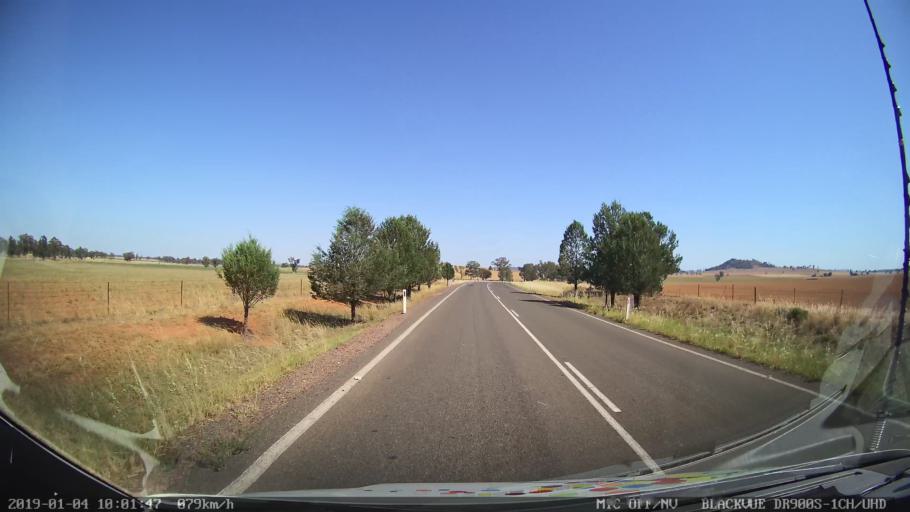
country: AU
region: New South Wales
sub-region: Cabonne
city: Canowindra
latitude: -33.4841
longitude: 148.3678
